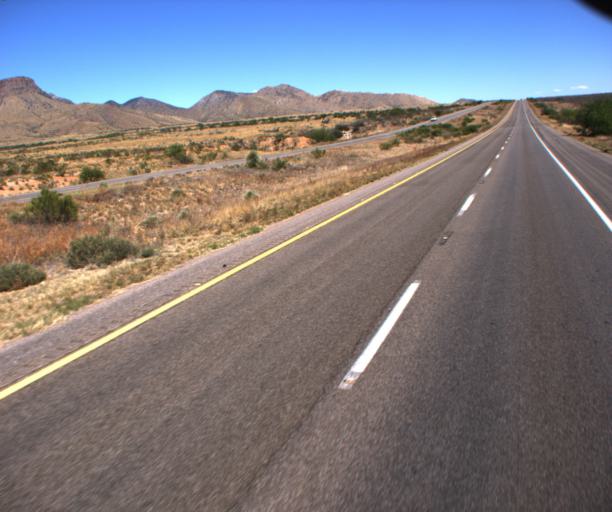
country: US
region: Arizona
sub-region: Cochise County
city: Huachuca City
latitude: 31.7890
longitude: -110.3499
